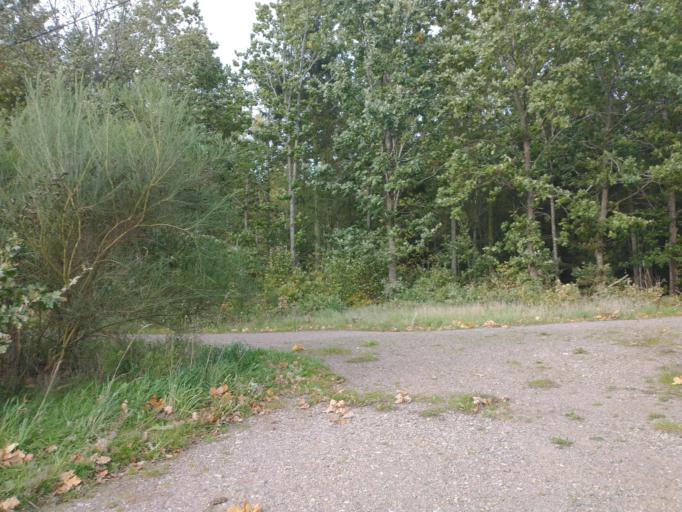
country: SE
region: Kalmar
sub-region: Kalmar Kommun
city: Lindsdal
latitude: 56.7739
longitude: 16.2999
